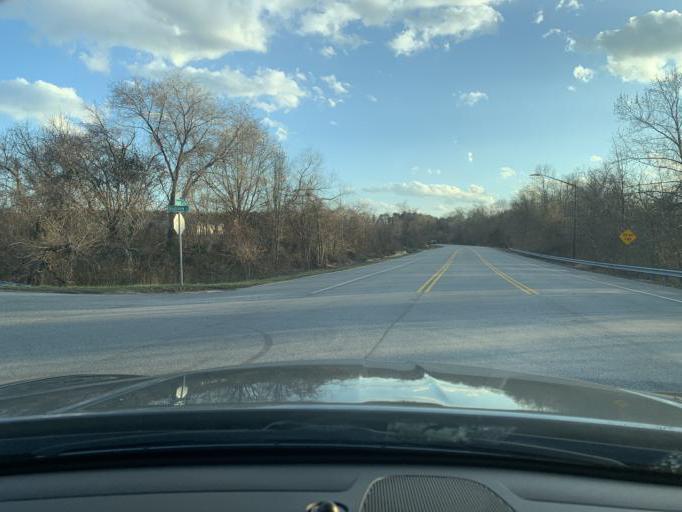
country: US
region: Maryland
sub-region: Anne Arundel County
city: South Gate
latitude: 39.1103
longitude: -76.6356
